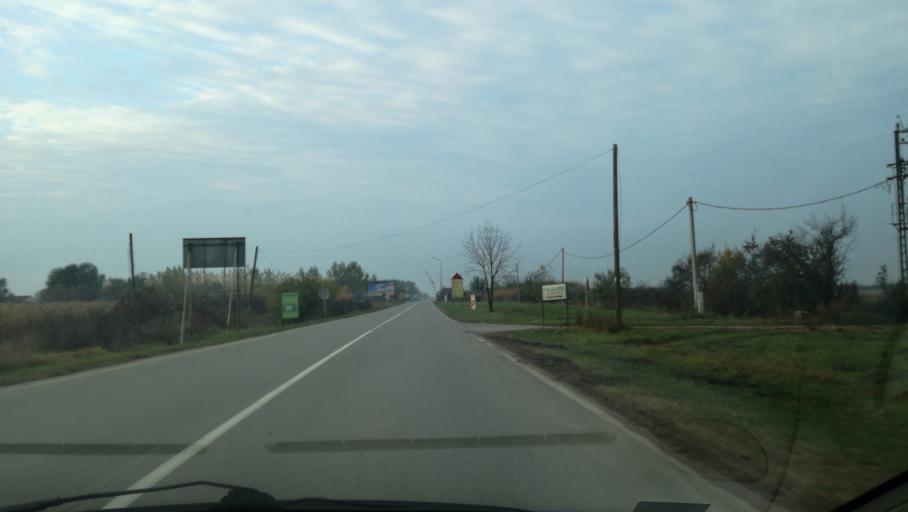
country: RS
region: Autonomna Pokrajina Vojvodina
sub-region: Severnobanatski Okrug
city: Kikinda
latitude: 45.7964
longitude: 20.4389
